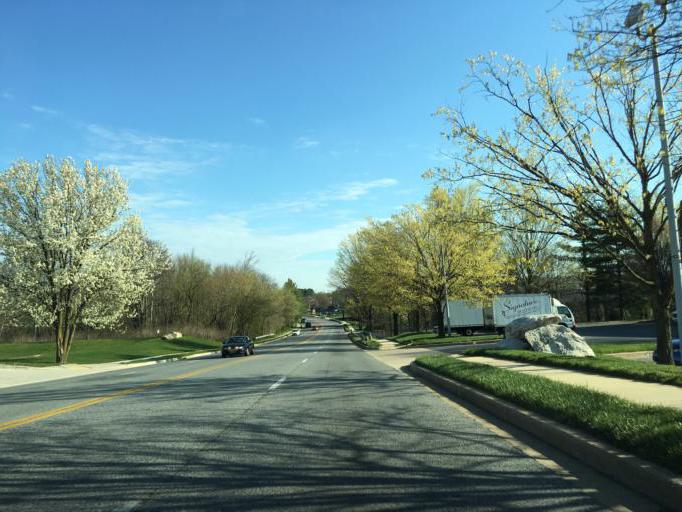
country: US
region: Maryland
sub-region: Baltimore County
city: Cockeysville
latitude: 39.4837
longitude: -76.6568
